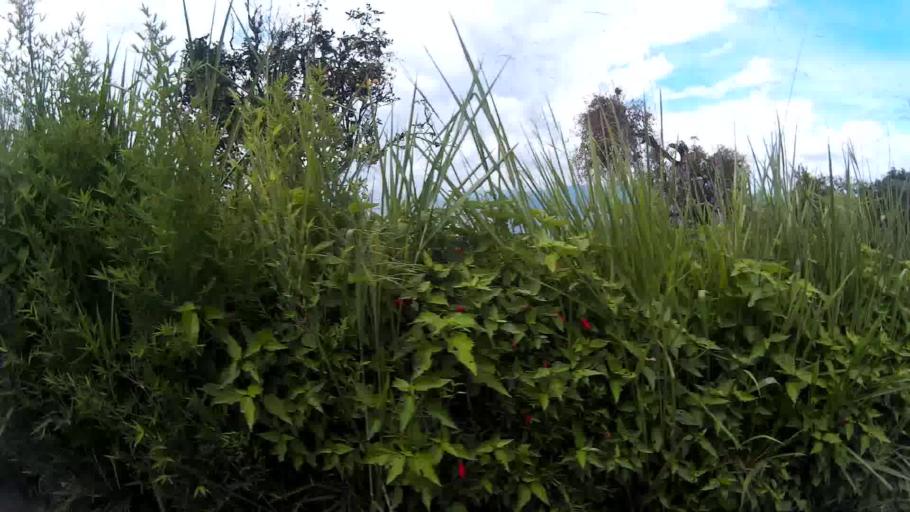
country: CO
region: Caldas
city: Belalcazar
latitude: 4.9823
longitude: -75.8147
